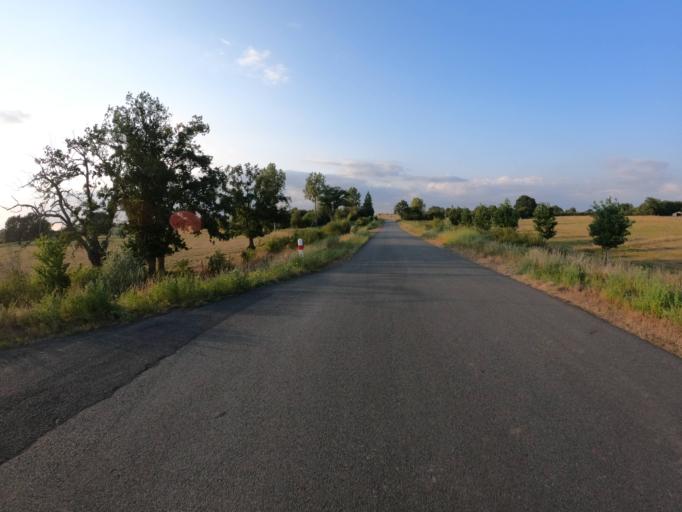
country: FR
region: Pays de la Loire
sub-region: Departement de la Sarthe
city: Brulon
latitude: 47.9114
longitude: -0.2292
